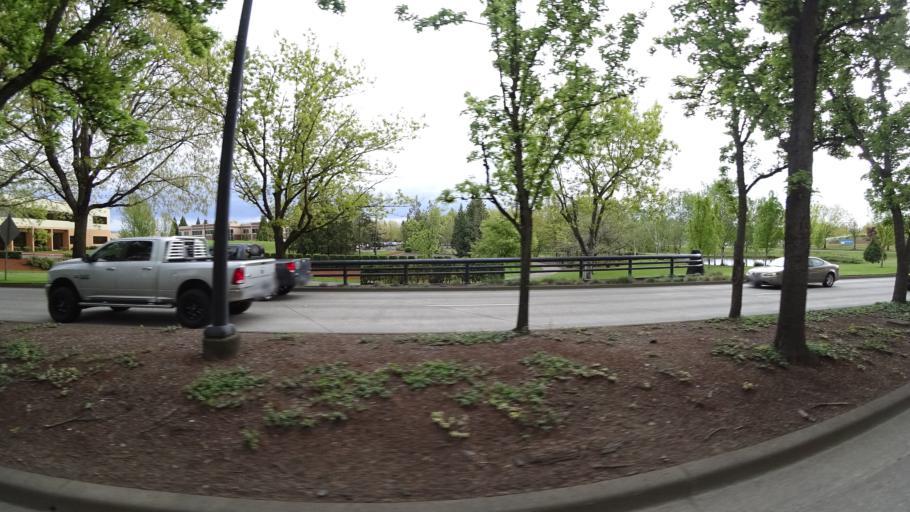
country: US
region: Oregon
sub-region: Washington County
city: Rockcreek
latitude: 45.5466
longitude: -122.9307
